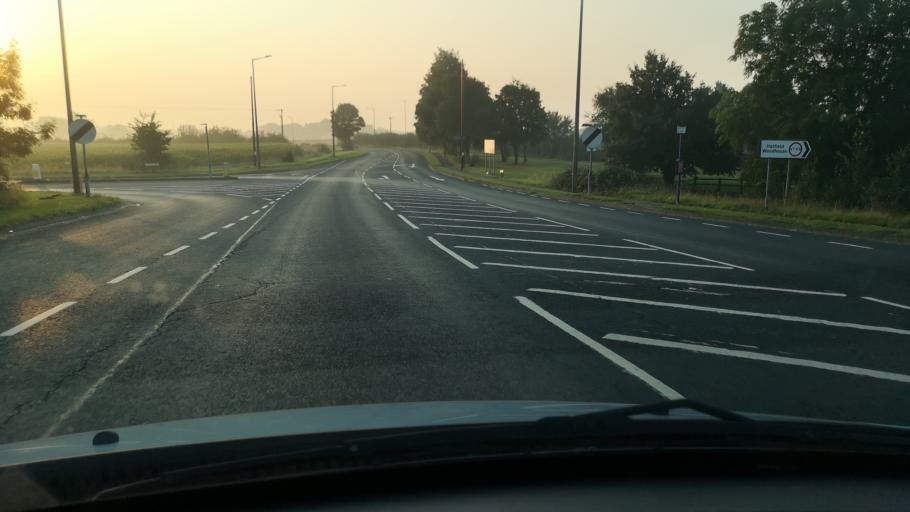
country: GB
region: England
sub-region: Doncaster
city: Hatfield
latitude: 53.5774
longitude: -0.9879
